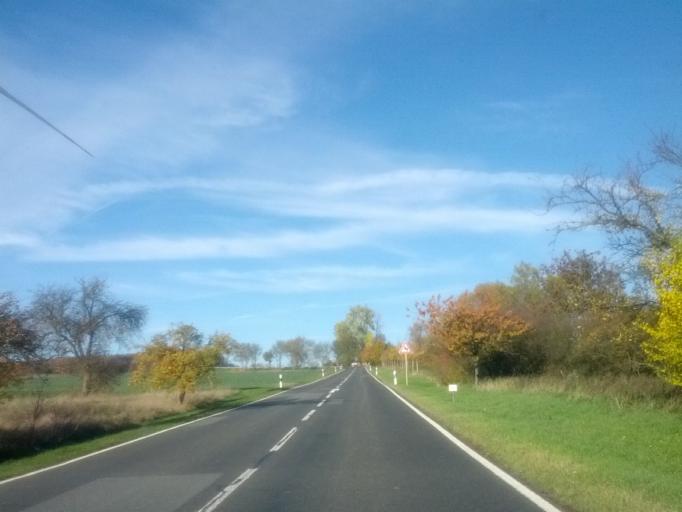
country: DE
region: Thuringia
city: Mechterstadt
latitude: 50.9549
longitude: 10.5571
